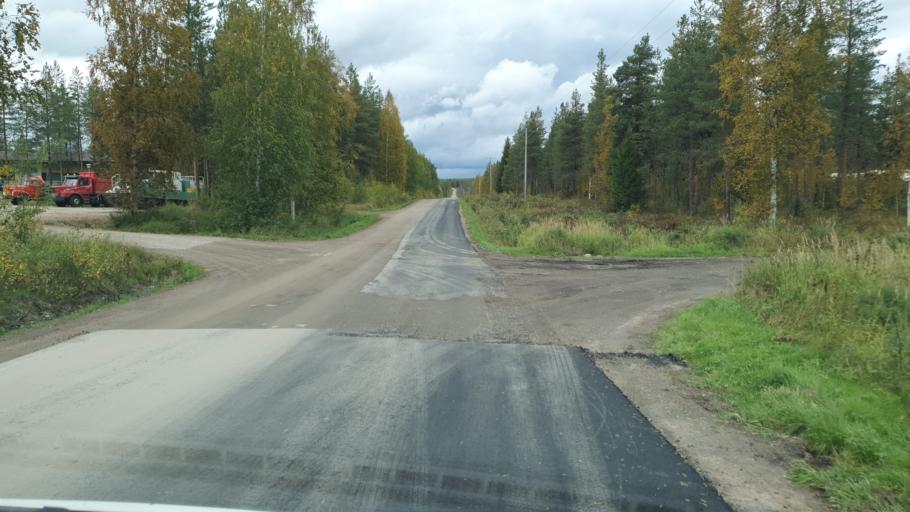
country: FI
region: Lapland
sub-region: Rovaniemi
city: Rovaniemi
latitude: 66.4267
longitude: 25.3968
